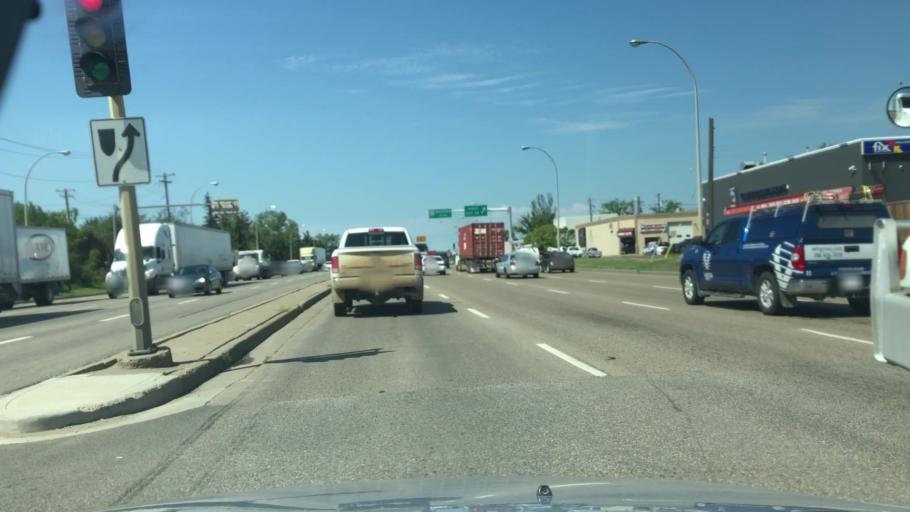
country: CA
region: Alberta
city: Edmonton
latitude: 53.5806
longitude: -113.5361
